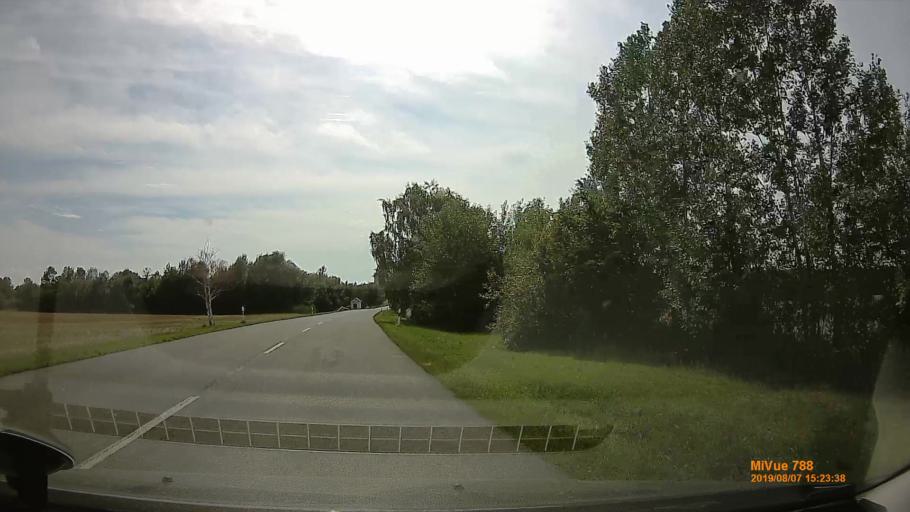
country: HU
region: Vas
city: Buk
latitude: 47.3171
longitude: 16.8384
